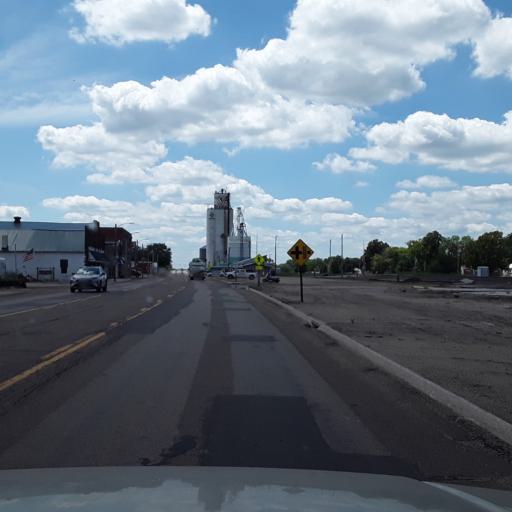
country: US
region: Nebraska
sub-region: Nance County
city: Genoa
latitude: 41.3164
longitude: -97.6616
